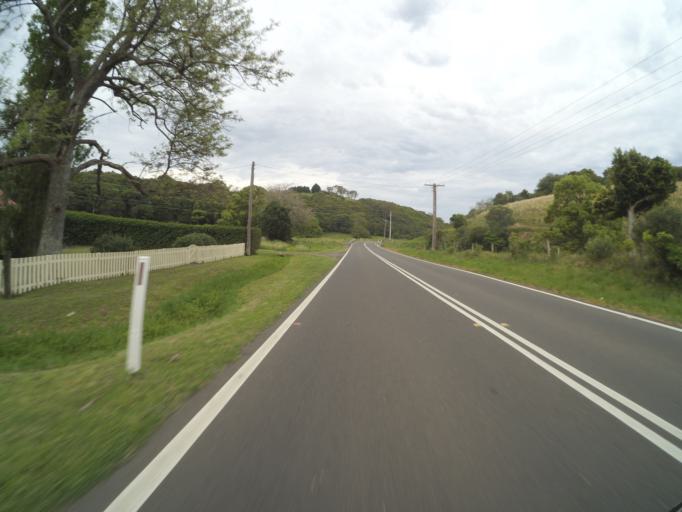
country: AU
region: New South Wales
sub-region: Kiama
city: Kiama
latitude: -34.6632
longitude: 150.8382
